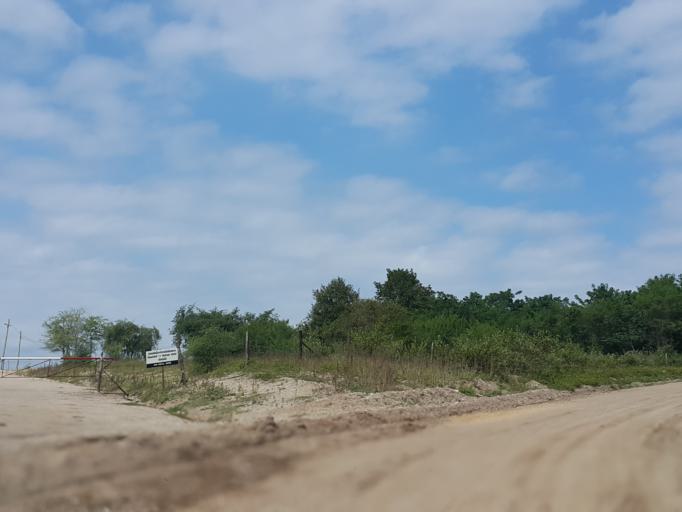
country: TH
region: Lampang
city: Mae Mo
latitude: 18.3344
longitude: 99.7541
